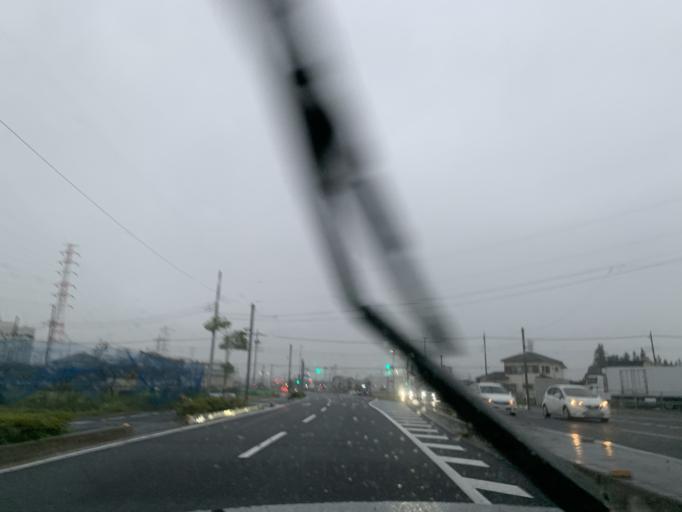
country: JP
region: Chiba
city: Nagareyama
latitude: 35.8439
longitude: 139.8735
